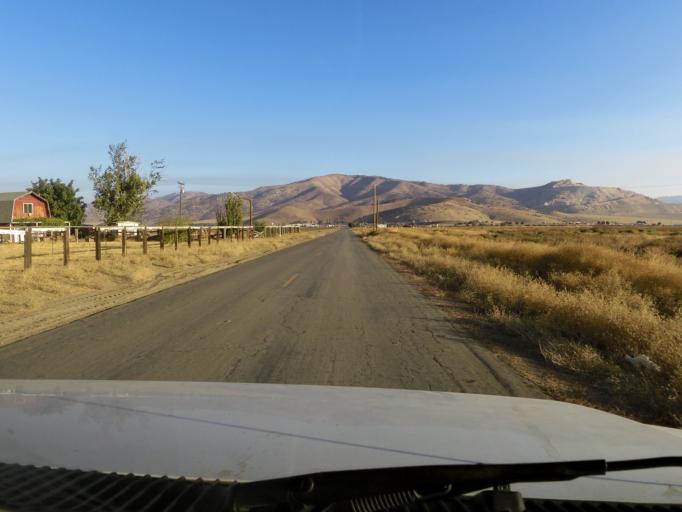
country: US
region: California
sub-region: Kern County
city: Tehachapi
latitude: 35.1159
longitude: -118.4144
